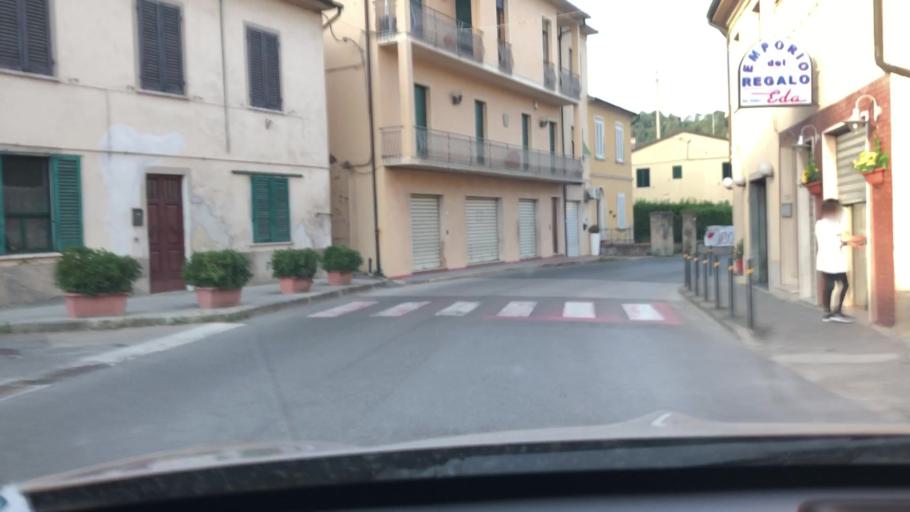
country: IT
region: Tuscany
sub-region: Province of Pisa
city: Forcoli
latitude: 43.6041
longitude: 10.7057
